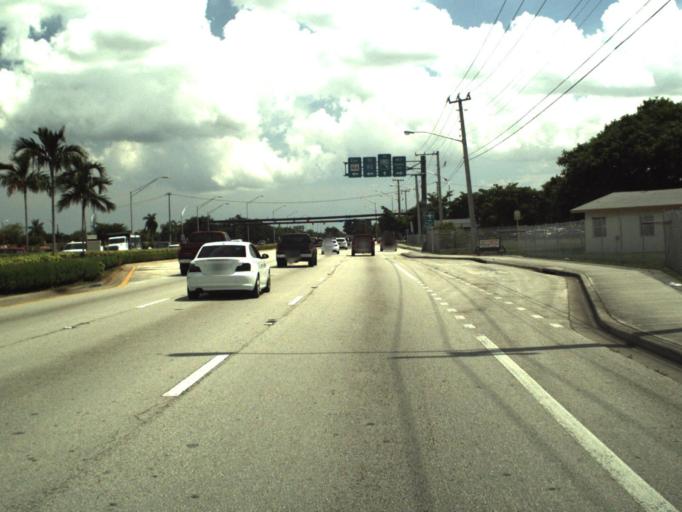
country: US
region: Florida
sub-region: Broward County
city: Miramar
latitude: 25.9971
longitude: -80.2479
